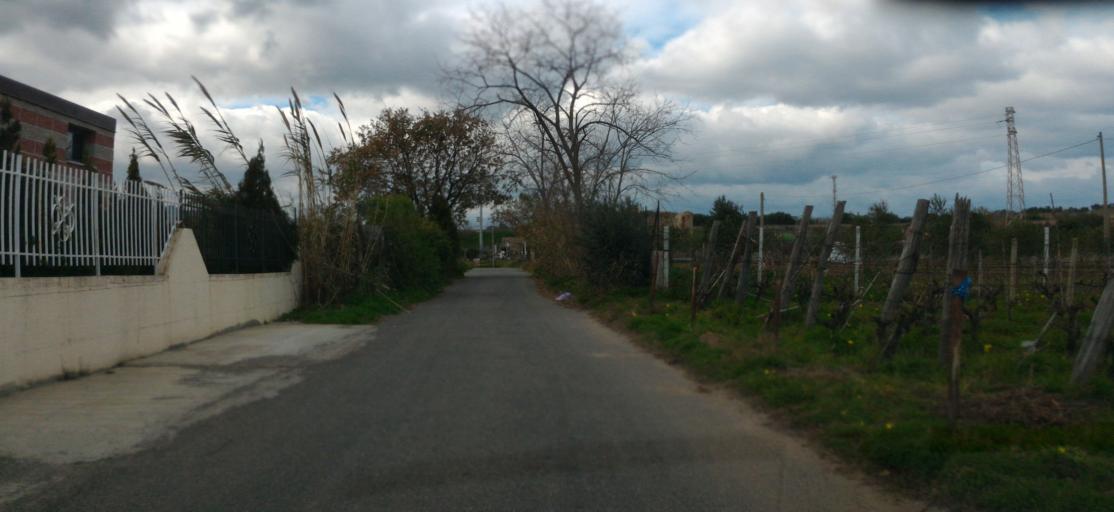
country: IT
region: Calabria
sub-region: Provincia di Crotone
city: Ciro Marina
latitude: 39.3895
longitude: 17.1255
